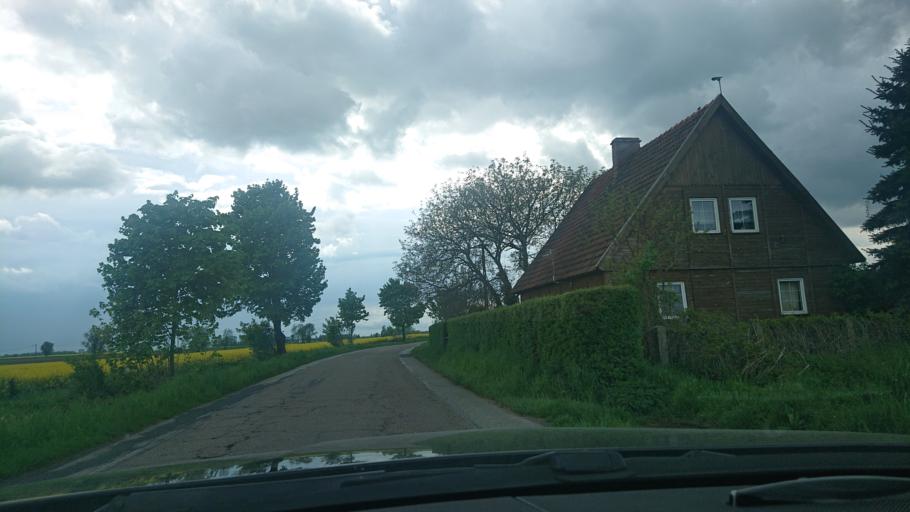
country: PL
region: Greater Poland Voivodeship
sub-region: Powiat gnieznienski
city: Niechanowo
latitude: 52.4784
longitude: 17.6522
